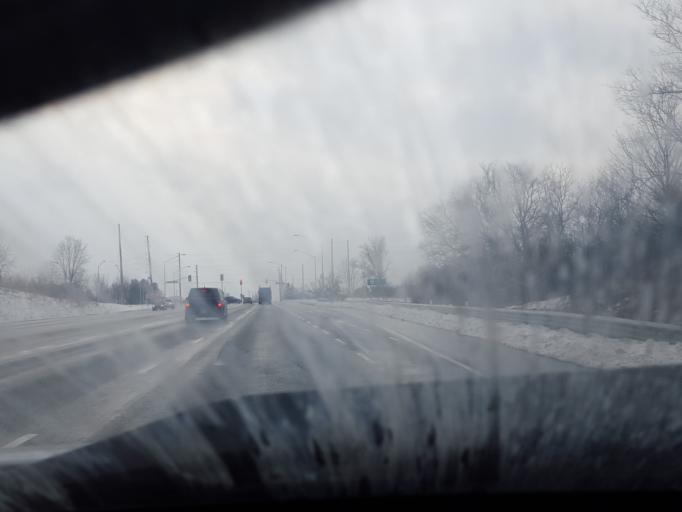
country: CA
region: Ontario
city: Newmarket
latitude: 43.9740
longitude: -79.4079
